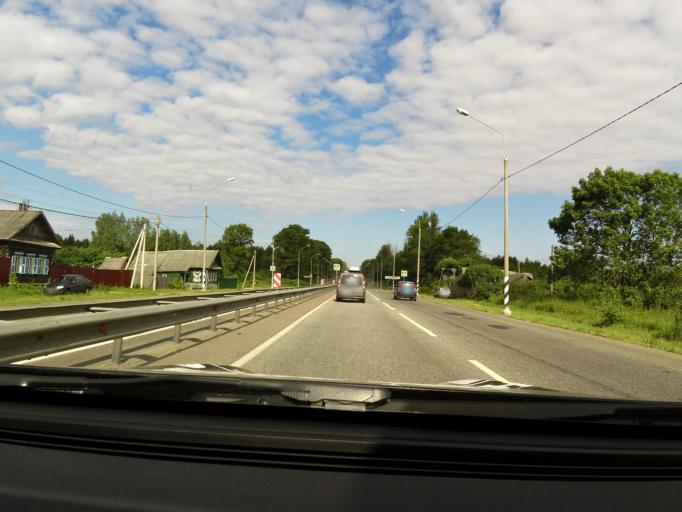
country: RU
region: Tverskaya
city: Gorodnya
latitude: 56.7393
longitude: 36.2459
